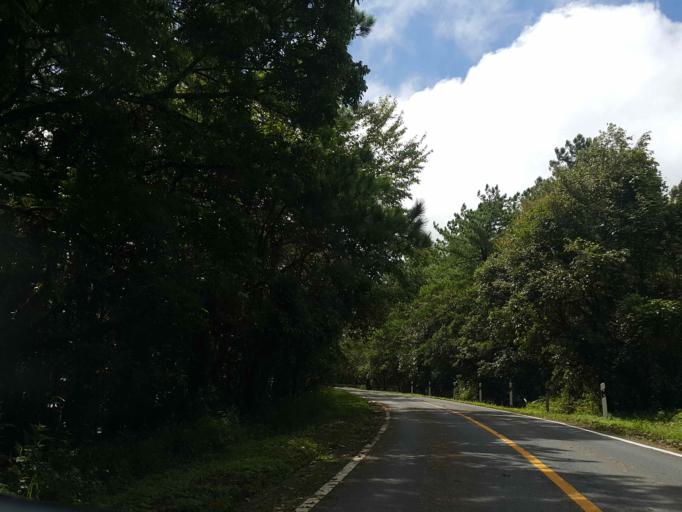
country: TH
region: Chiang Mai
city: Mae Chaem
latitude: 18.5420
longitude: 98.4882
